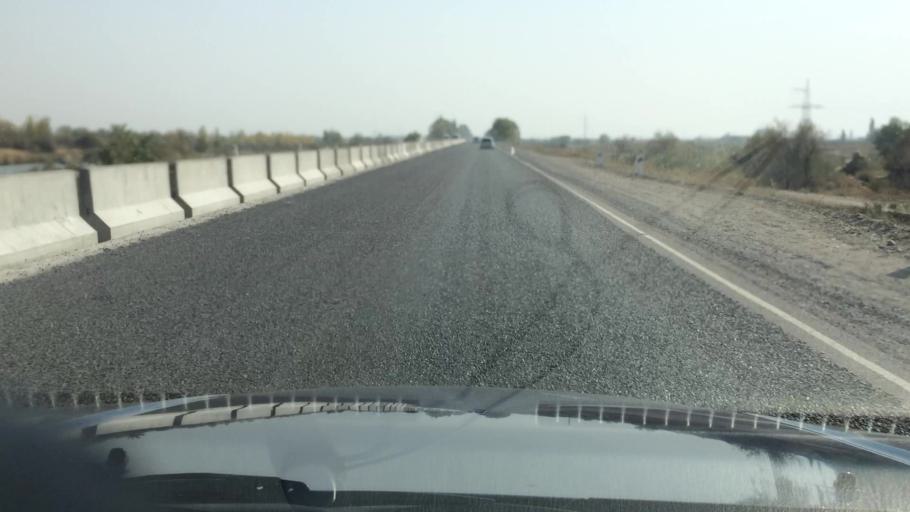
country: KG
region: Chuy
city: Kant
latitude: 42.9716
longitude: 74.9007
